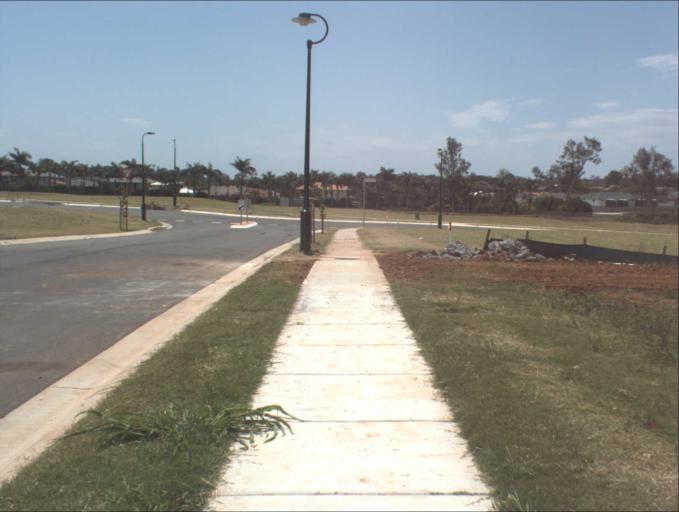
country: AU
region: Queensland
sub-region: Logan
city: Rochedale South
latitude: -27.6006
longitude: 153.1066
